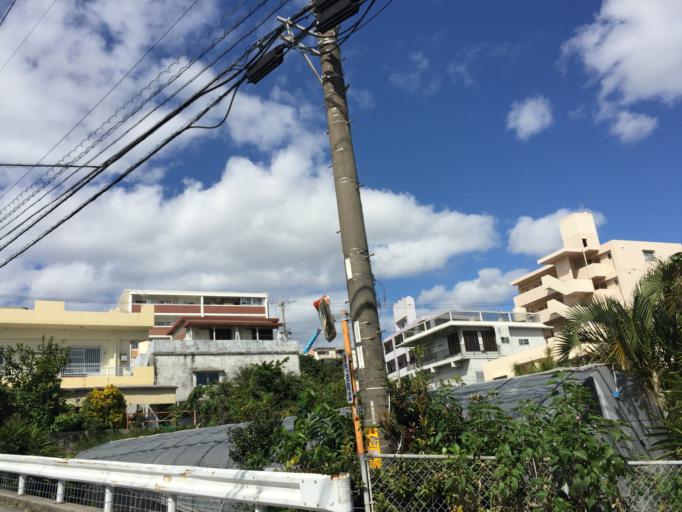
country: JP
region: Okinawa
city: Ginowan
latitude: 26.2358
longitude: 127.7329
